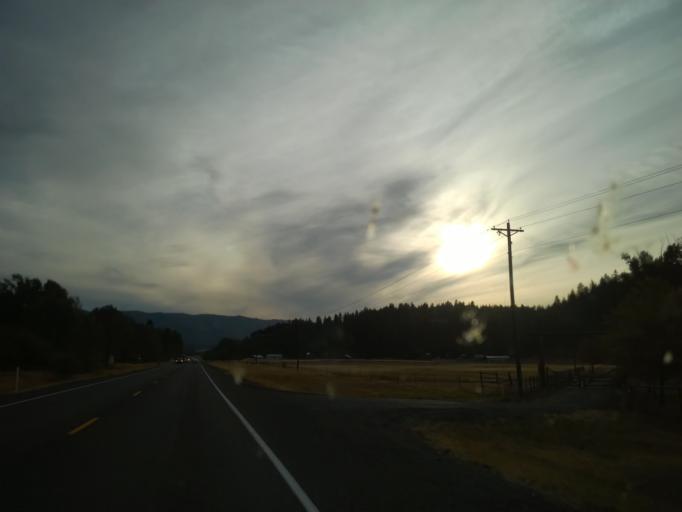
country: US
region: Washington
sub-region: Kittitas County
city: Cle Elum
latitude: 47.1890
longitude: -120.8175
